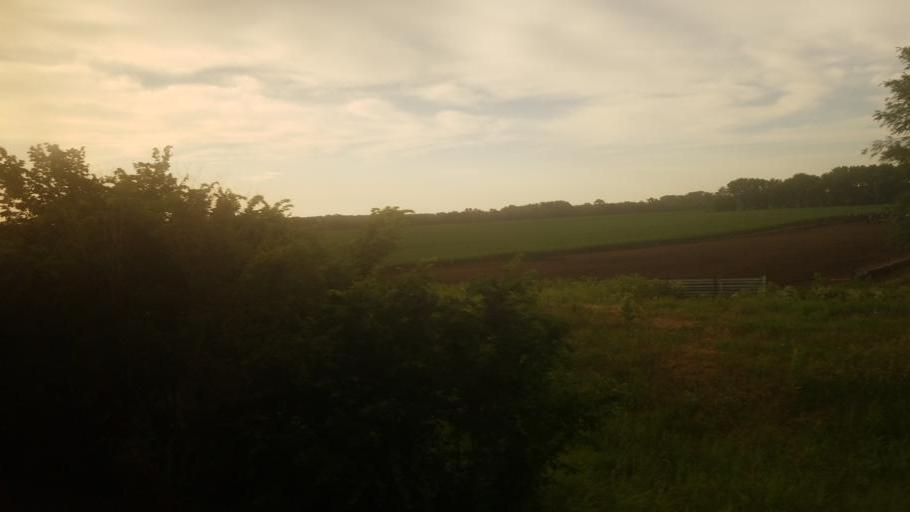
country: US
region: Kansas
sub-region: Osage County
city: Osage City
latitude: 38.5194
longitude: -95.9486
